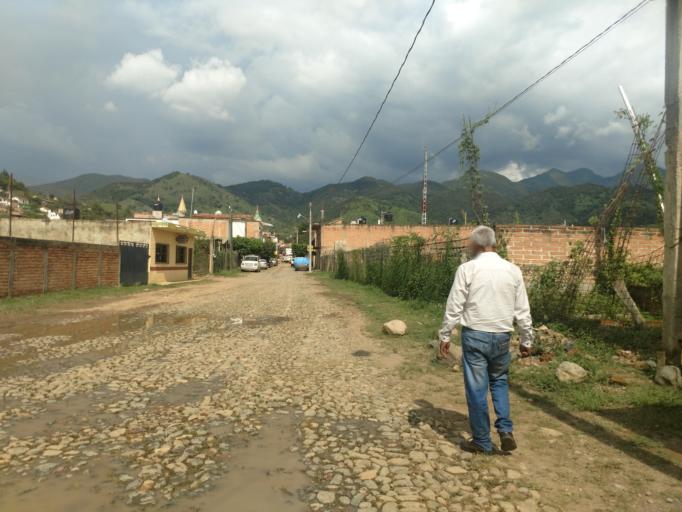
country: MX
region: Jalisco
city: Talpa de Allende
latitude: 20.3794
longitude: -104.8253
